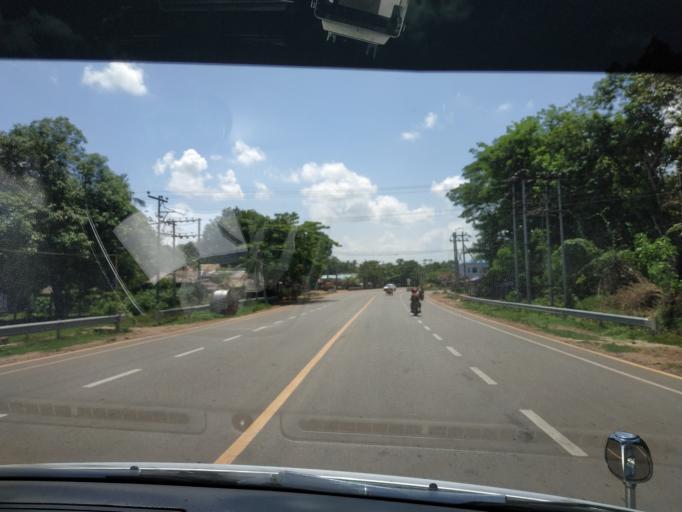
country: MM
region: Mon
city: Kyaikto
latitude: 17.3138
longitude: 97.0195
